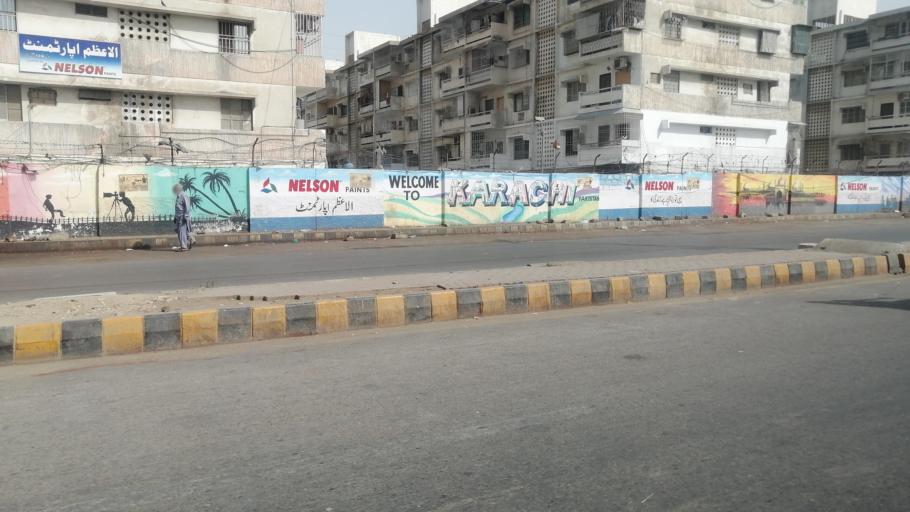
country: PK
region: Sindh
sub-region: Karachi District
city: Karachi
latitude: 24.9022
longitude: 67.0745
